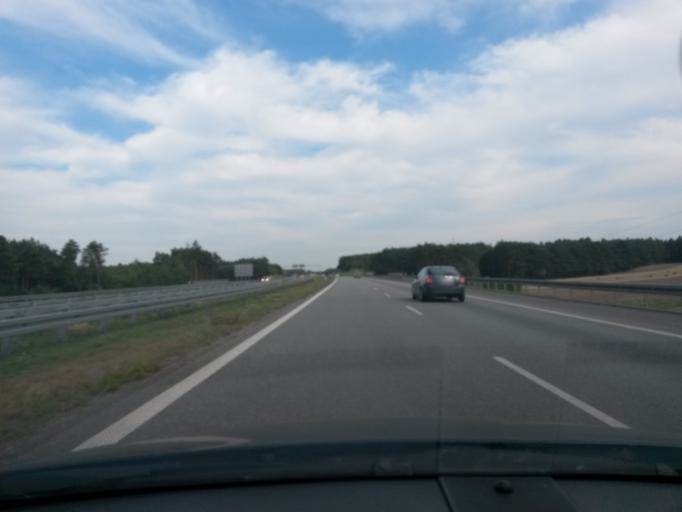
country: PL
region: Greater Poland Voivodeship
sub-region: Powiat turecki
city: Tuliszkow
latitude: 52.1495
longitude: 18.2902
